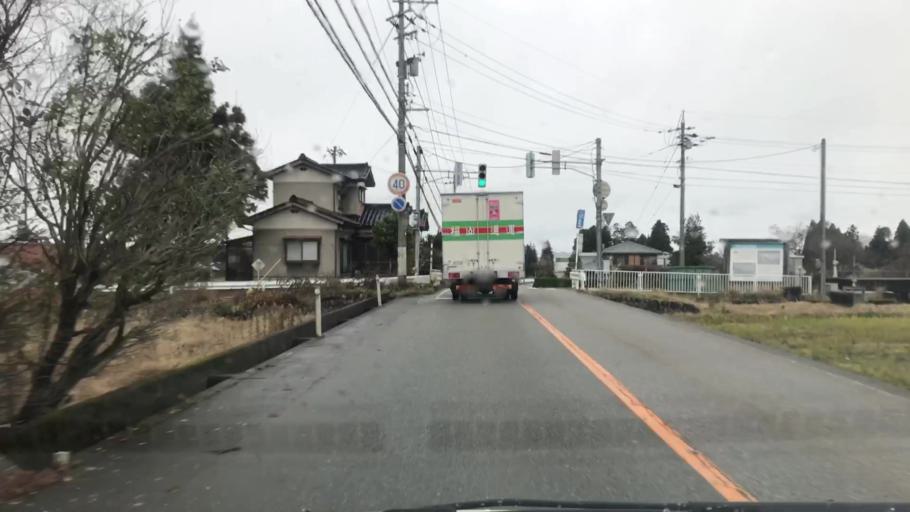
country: JP
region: Toyama
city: Kamiichi
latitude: 36.6012
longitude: 137.3218
